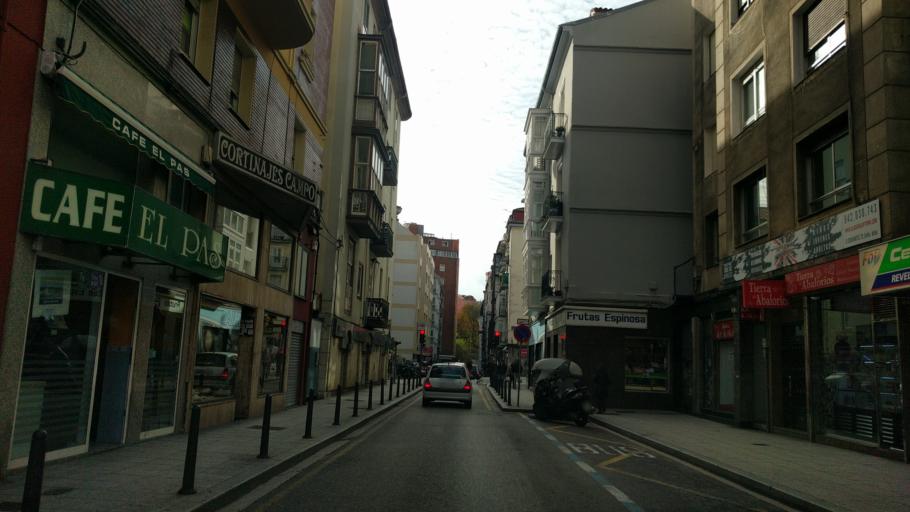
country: ES
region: Cantabria
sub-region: Provincia de Cantabria
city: Santander
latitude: 43.4637
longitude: -3.8113
